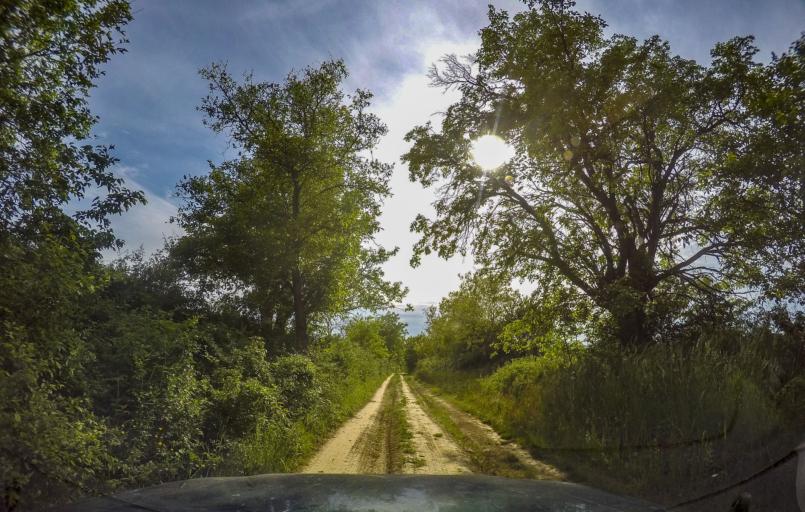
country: HU
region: Somogy
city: Karad
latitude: 46.7136
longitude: 17.8927
